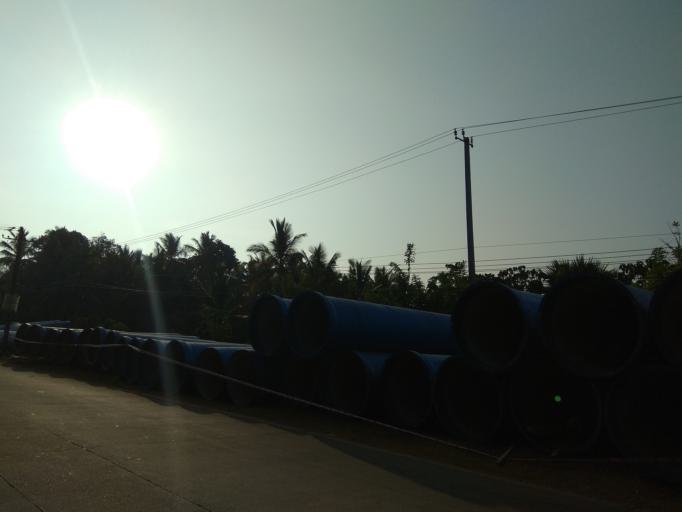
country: IN
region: Karnataka
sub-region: Dakshina Kannada
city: Mangalore
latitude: 12.9132
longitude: 74.8555
